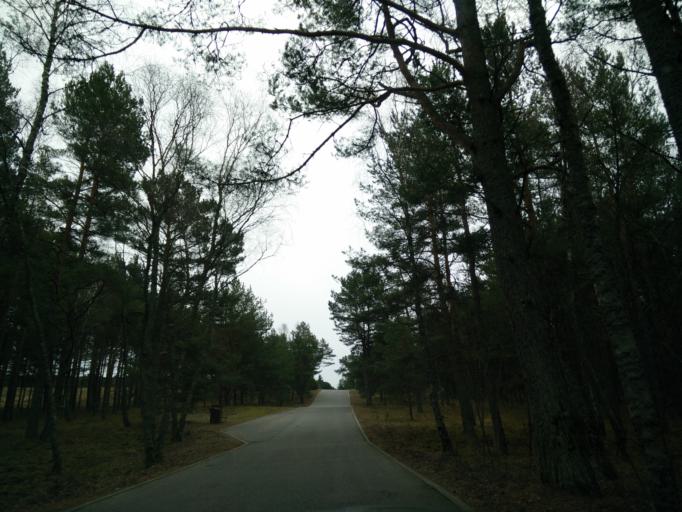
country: LT
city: Nida
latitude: 55.2981
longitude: 20.9847
